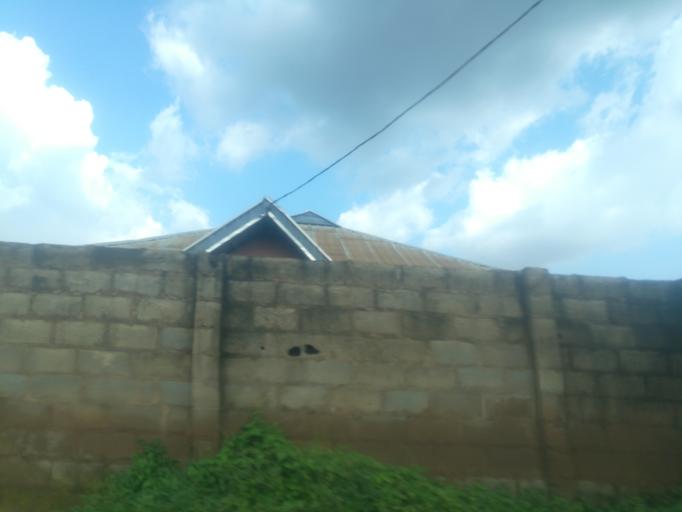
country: NG
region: Oyo
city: Ibadan
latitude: 7.3998
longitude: 3.8358
